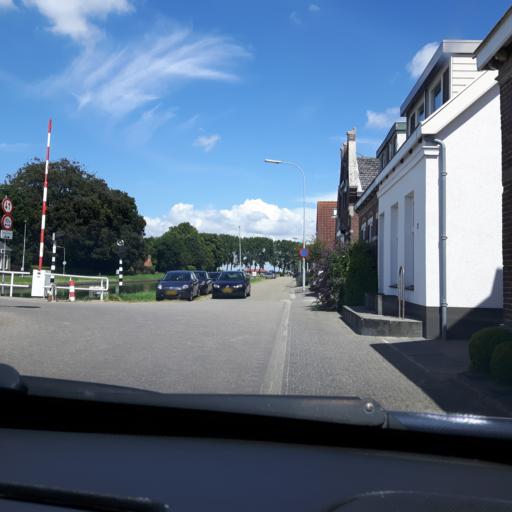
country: NL
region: Zeeland
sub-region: Gemeente Goes
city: Goes
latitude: 51.5295
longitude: 3.8996
